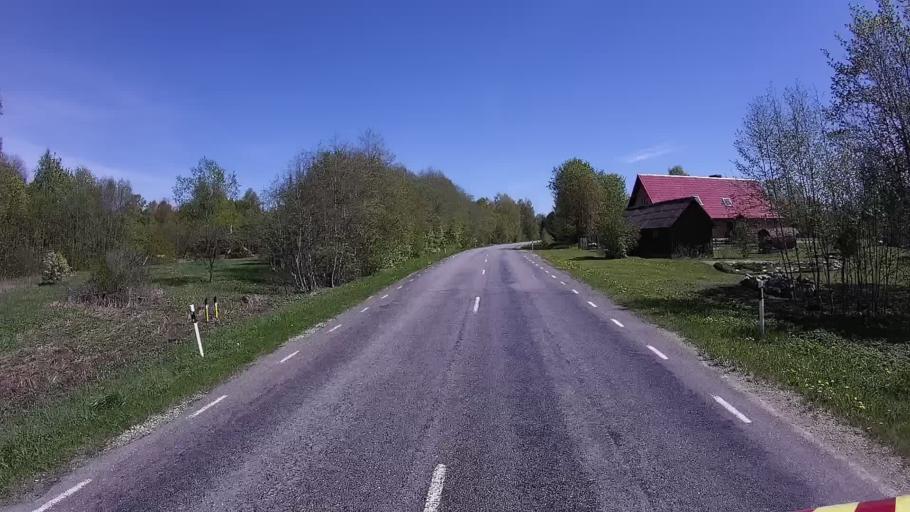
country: EE
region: Raplamaa
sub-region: Kehtna vald
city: Kehtna
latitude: 59.0536
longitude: 25.0112
